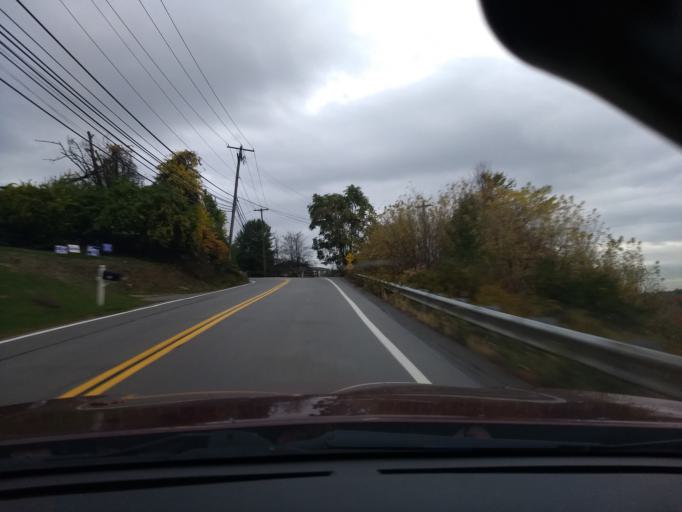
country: US
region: Pennsylvania
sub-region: Allegheny County
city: Jefferson Hills
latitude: 40.3044
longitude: -79.9421
